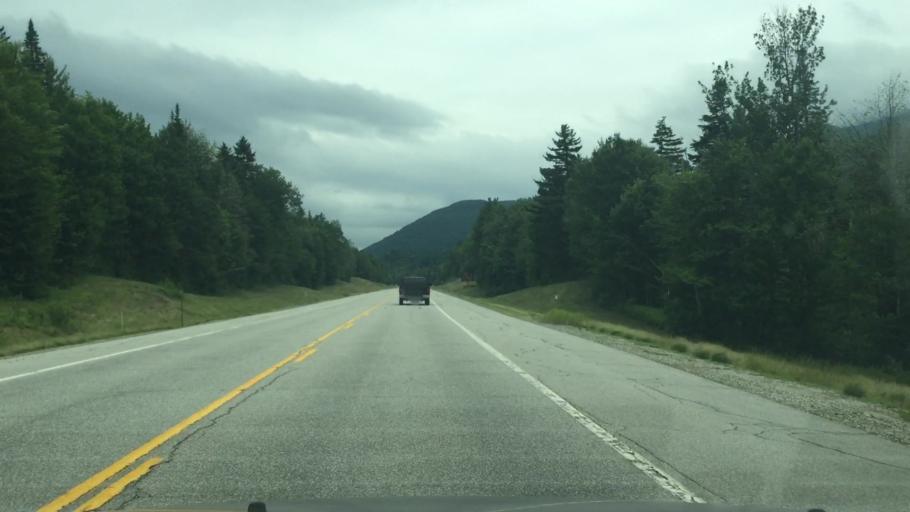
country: US
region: New Hampshire
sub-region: Coos County
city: Jefferson
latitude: 44.2358
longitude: -71.4226
